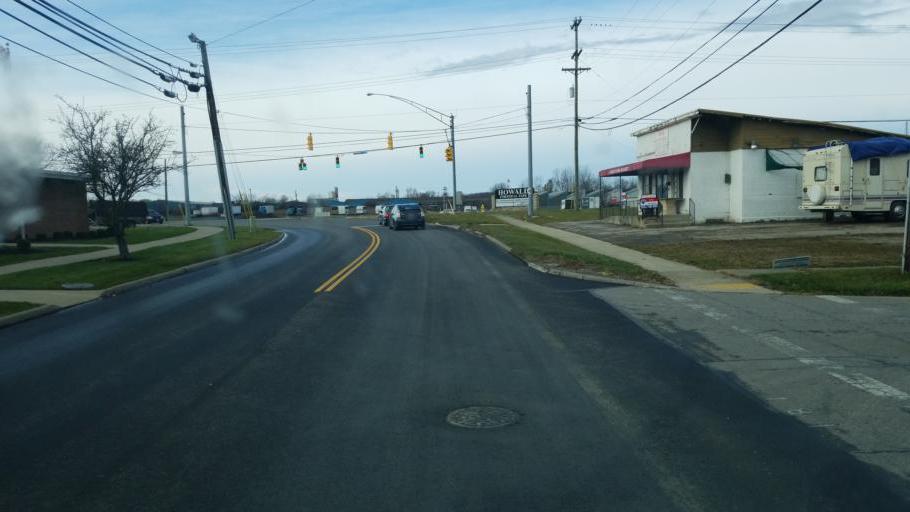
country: US
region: Ohio
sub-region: Delaware County
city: Delaware
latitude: 40.2908
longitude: -83.0789
